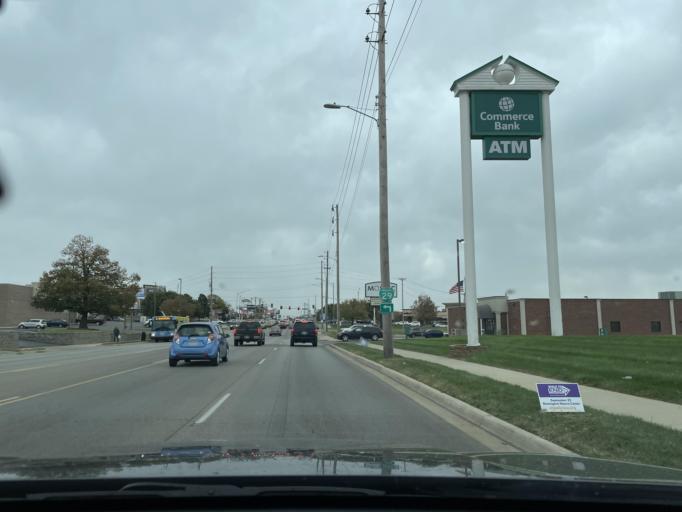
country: US
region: Missouri
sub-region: Buchanan County
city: Saint Joseph
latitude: 39.7769
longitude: -94.8054
